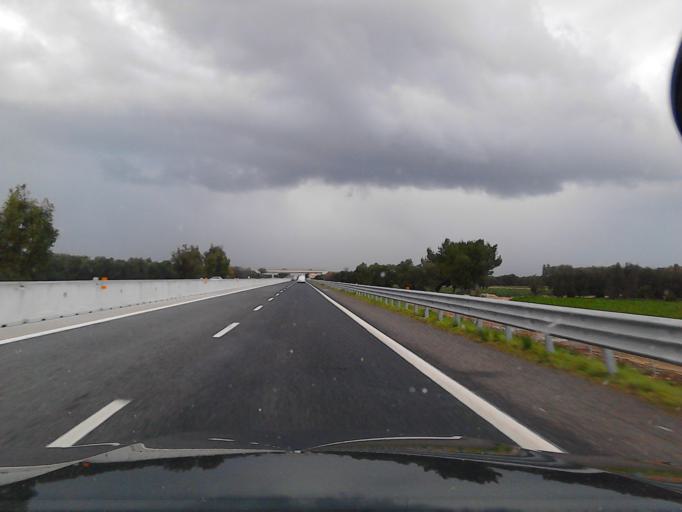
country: IT
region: Apulia
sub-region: Provincia di Bari
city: Bitonto
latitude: 41.1205
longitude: 16.7273
